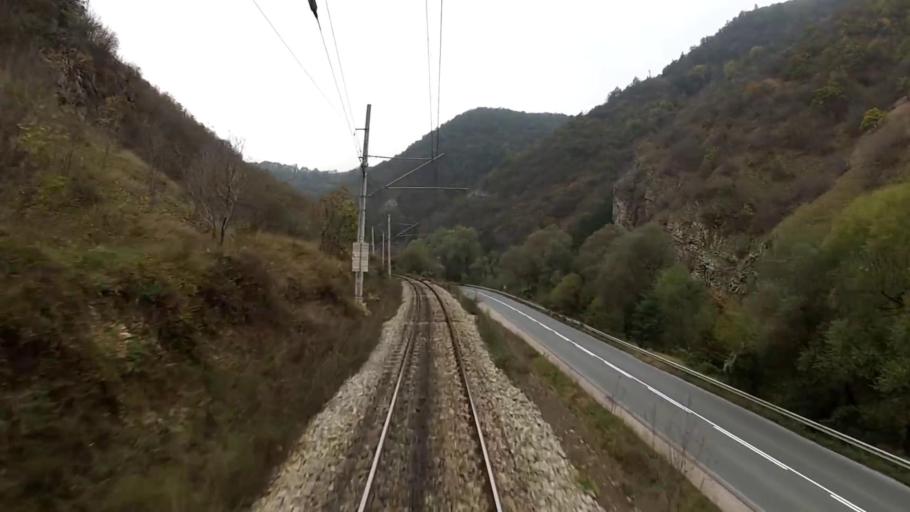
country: RS
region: Central Serbia
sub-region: Pirotski Okrug
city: Dimitrovgrad
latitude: 42.9732
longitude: 22.8507
